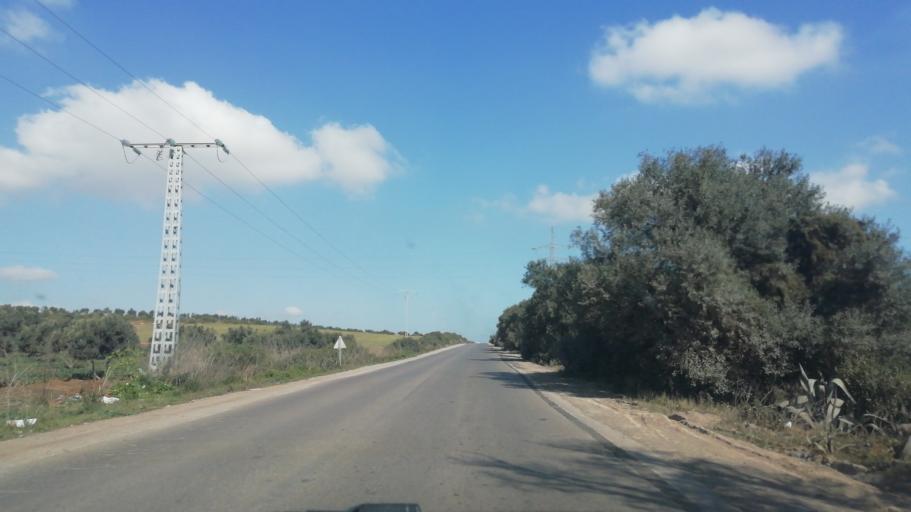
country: DZ
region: Oran
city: Ain el Bya
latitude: 35.7618
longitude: -0.2758
